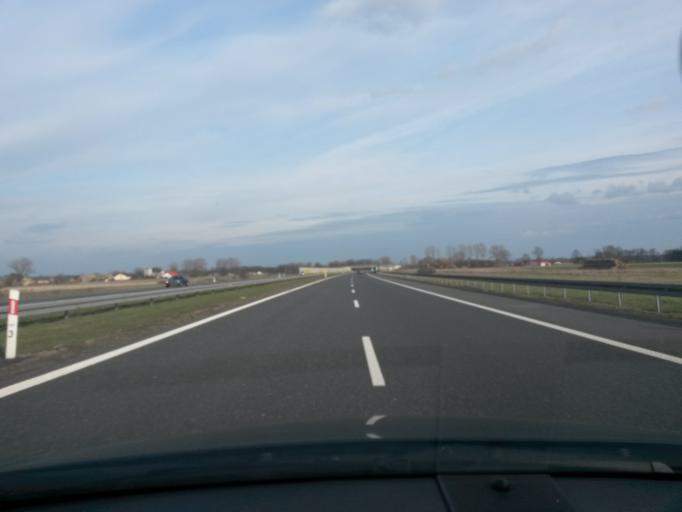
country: PL
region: Lodz Voivodeship
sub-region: Powiat poddebicki
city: Wartkowice
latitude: 52.0122
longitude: 18.9630
